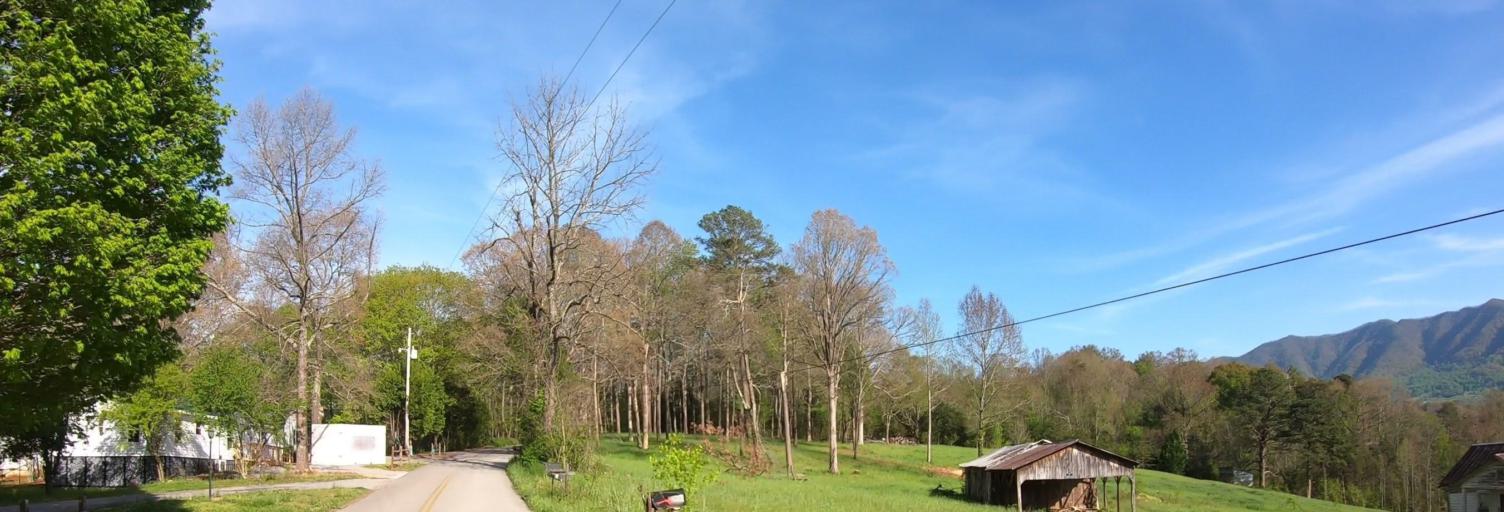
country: US
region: Tennessee
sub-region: Blount County
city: Wildwood
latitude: 35.6763
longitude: -83.7843
